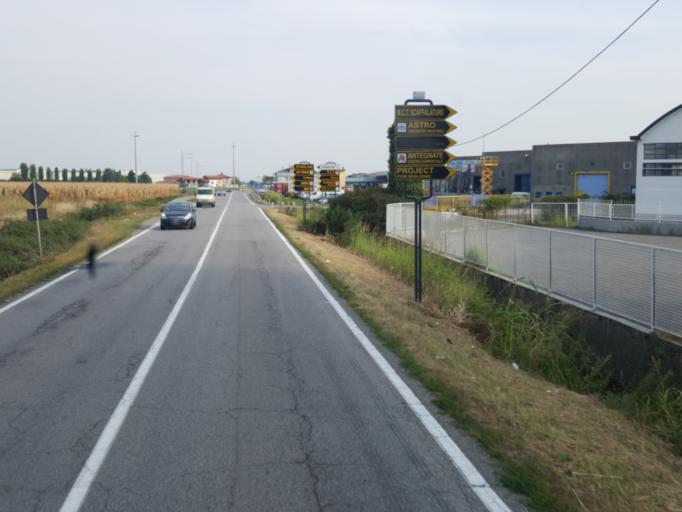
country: IT
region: Lombardy
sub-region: Provincia di Bergamo
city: Mornico al Serio
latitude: 45.6047
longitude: 9.8036
